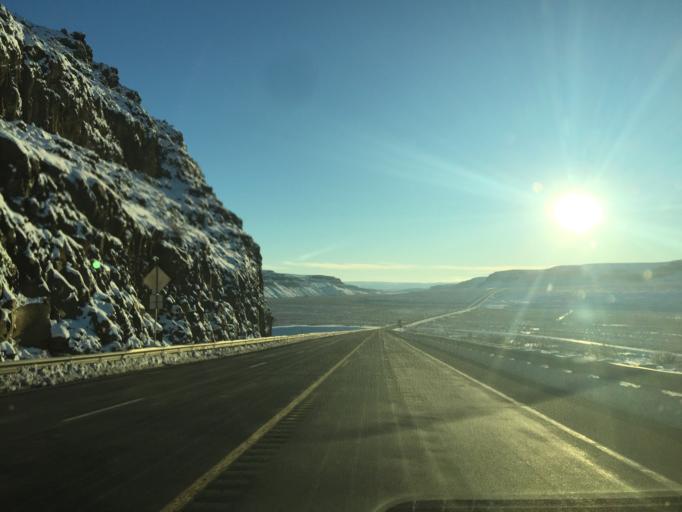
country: US
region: Washington
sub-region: Grant County
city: Soap Lake
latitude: 47.6045
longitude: -119.6661
